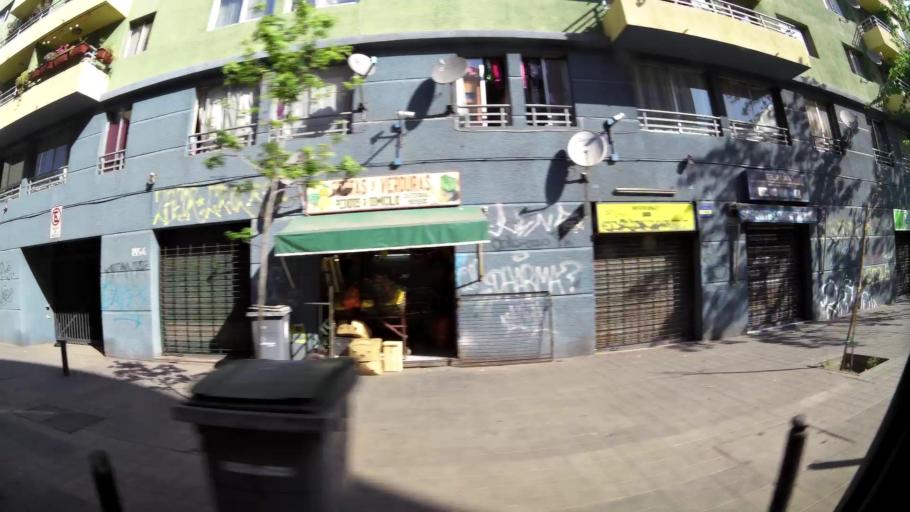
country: CL
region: Santiago Metropolitan
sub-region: Provincia de Santiago
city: Santiago
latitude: -33.4389
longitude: -70.6644
